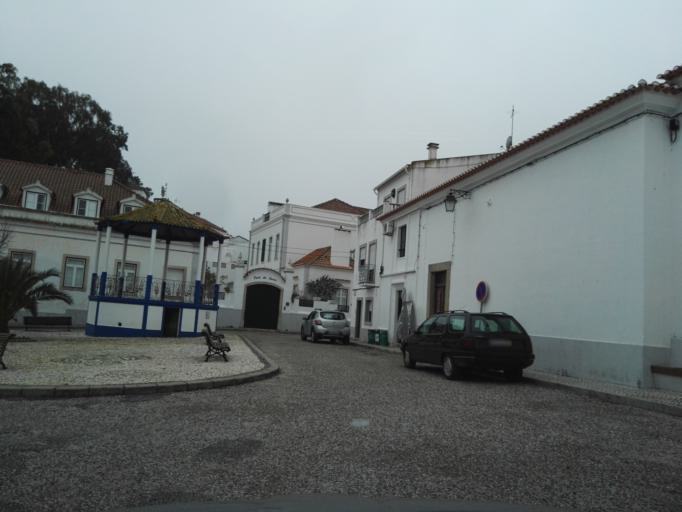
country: PT
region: Evora
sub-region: Vendas Novas
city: Vendas Novas
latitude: 38.7756
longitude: -8.3664
